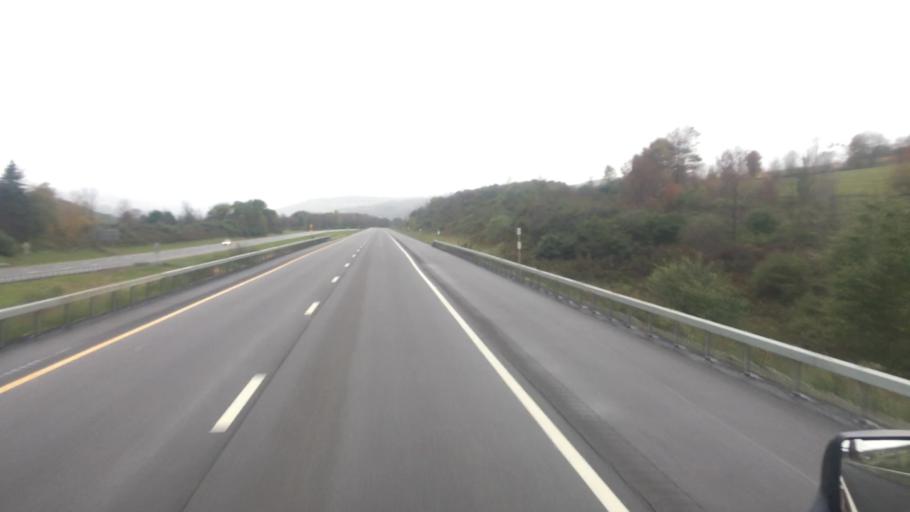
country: US
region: New York
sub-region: Broome County
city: Chenango Bridge
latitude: 42.1839
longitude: -75.7242
